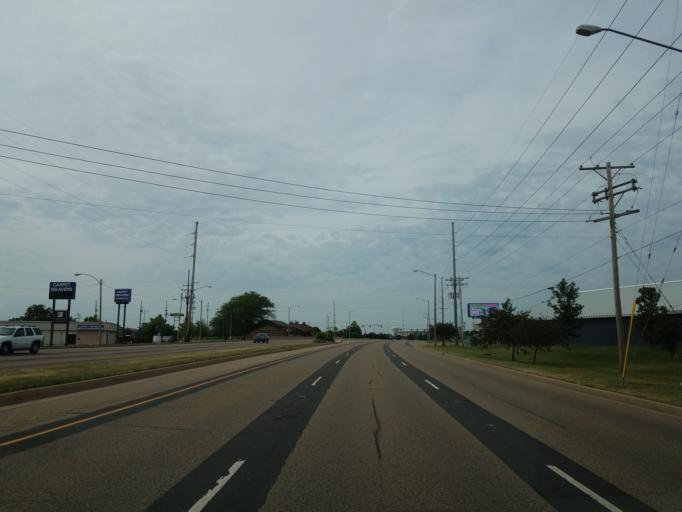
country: US
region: Illinois
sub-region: McLean County
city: Bloomington
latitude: 40.4687
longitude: -88.9537
